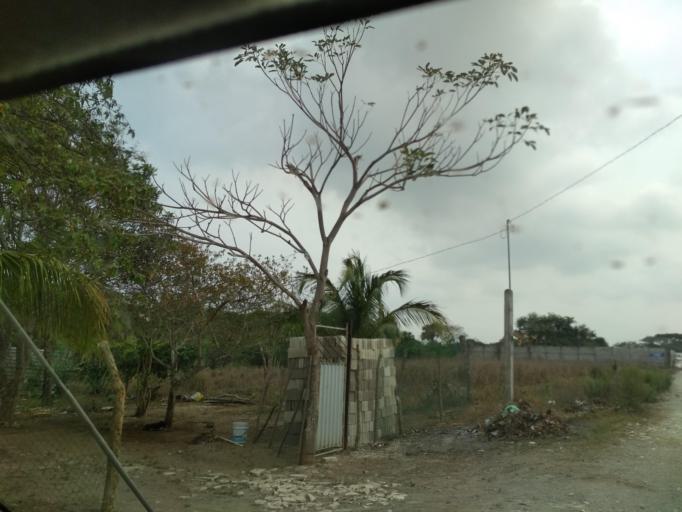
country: MX
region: Veracruz
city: Paso del Toro
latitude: 19.0111
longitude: -96.1153
